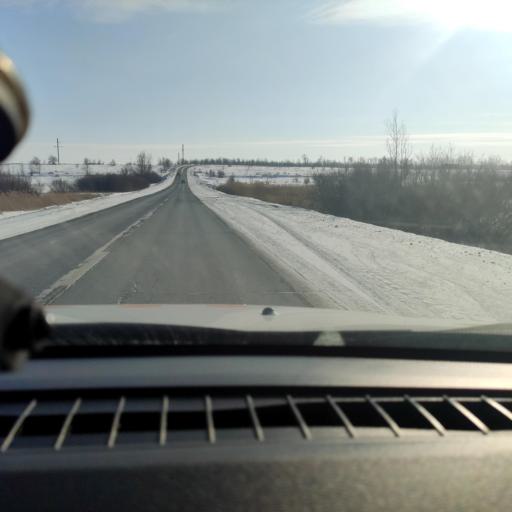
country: RU
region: Samara
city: Smyshlyayevka
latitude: 53.1589
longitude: 50.4569
